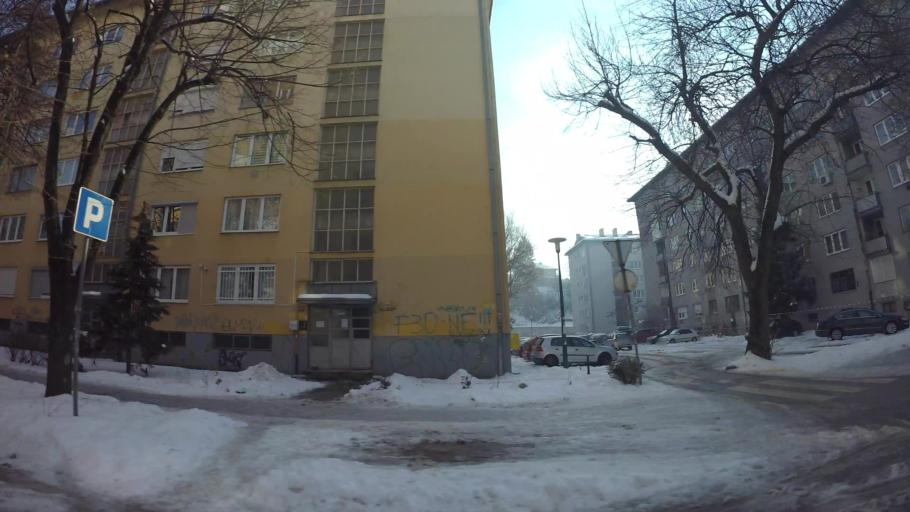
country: BA
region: Federation of Bosnia and Herzegovina
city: Kobilja Glava
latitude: 43.8492
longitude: 18.3910
